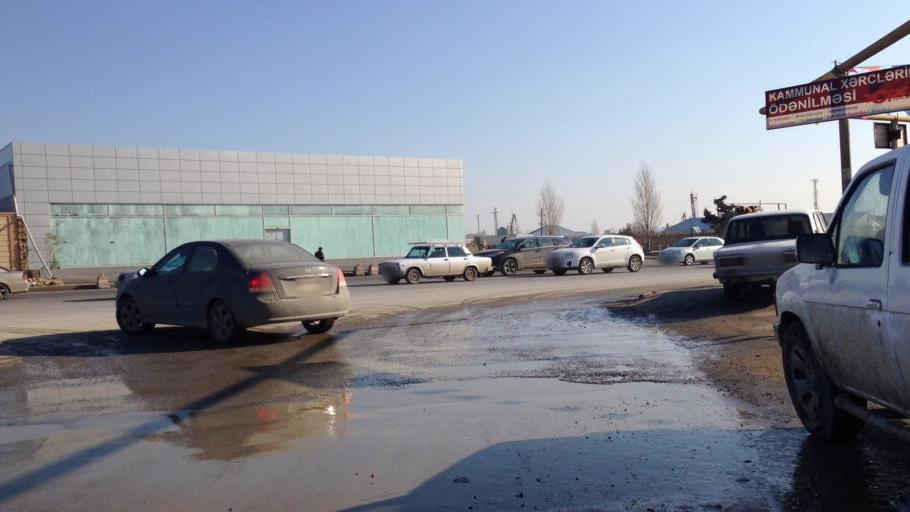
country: AZ
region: Baki
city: Sabuncu
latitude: 40.4464
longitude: 49.9342
